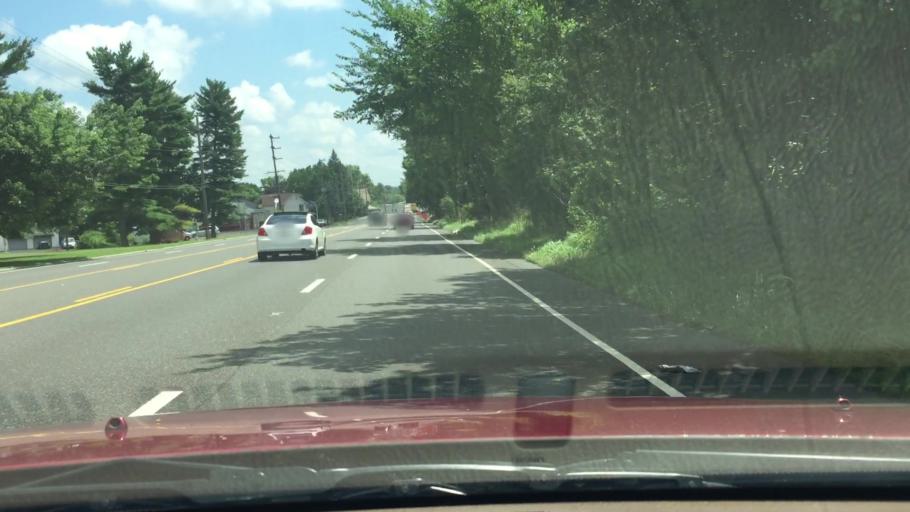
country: US
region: Pennsylvania
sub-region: Montgomery County
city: Horsham
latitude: 40.1866
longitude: -75.1339
